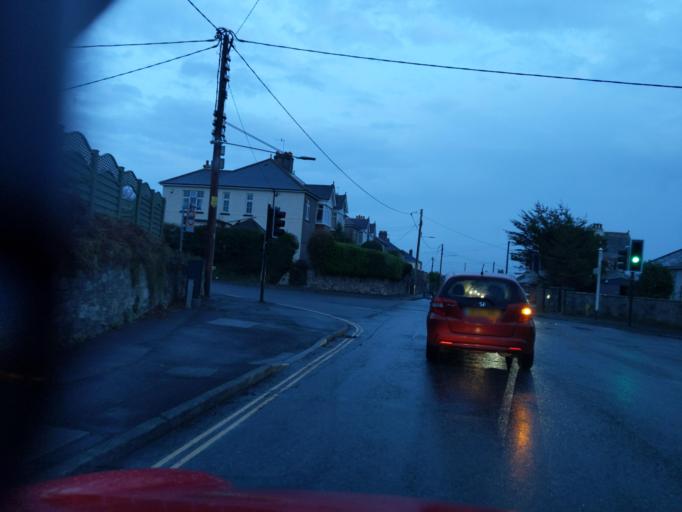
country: GB
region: England
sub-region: Plymouth
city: Plymstock
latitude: 50.3579
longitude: -4.0731
